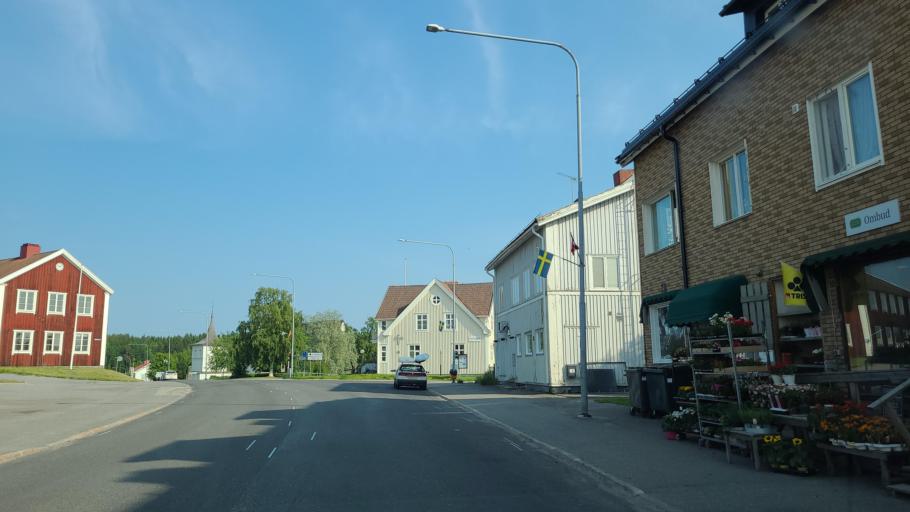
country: SE
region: Vaesterbotten
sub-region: Skelleftea Kommun
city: Burea
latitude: 64.3694
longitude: 21.3143
